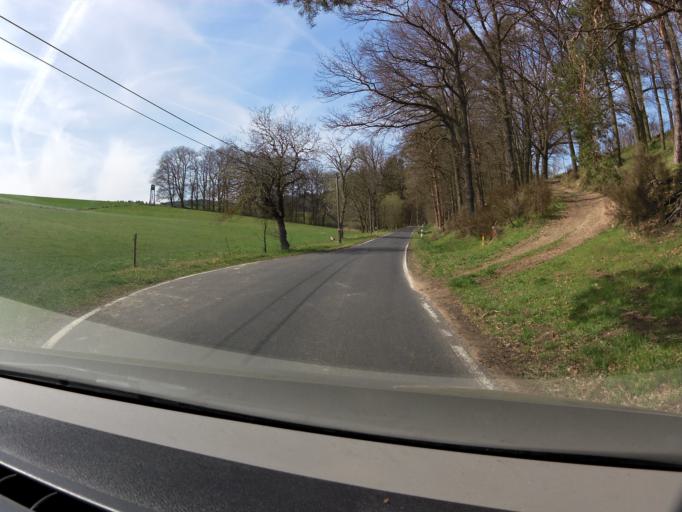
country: DE
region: Thuringia
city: Frauensee
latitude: 50.8648
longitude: 10.1404
